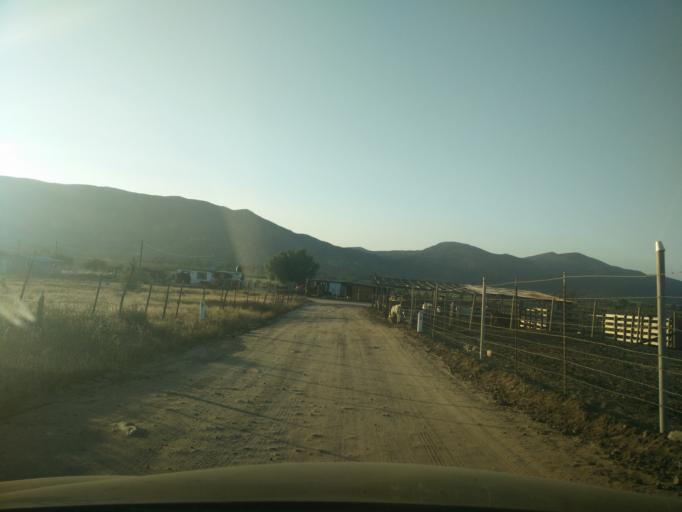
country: MX
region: Baja California
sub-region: Ensenada
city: Rancho Verde
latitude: 32.0472
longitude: -116.6457
